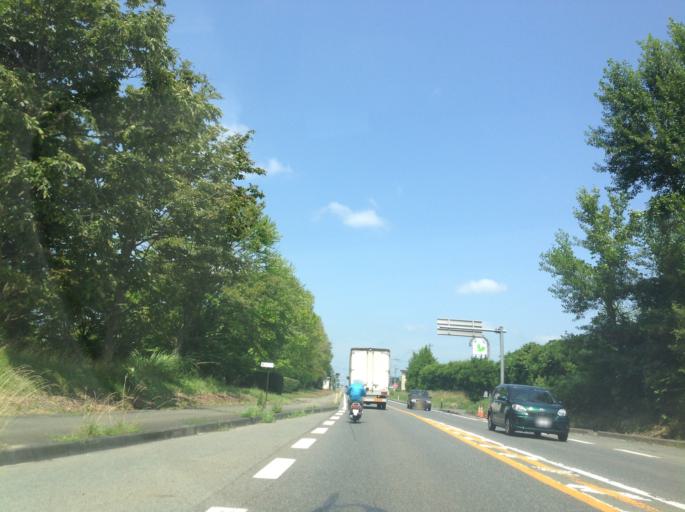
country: JP
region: Iwate
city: Hanamaki
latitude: 39.3522
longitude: 141.1099
